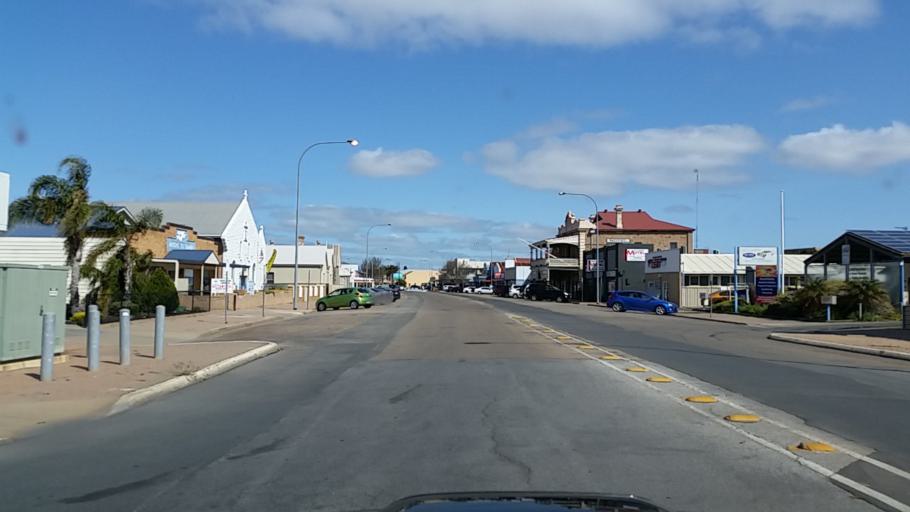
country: AU
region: South Australia
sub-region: Port Pirie City and Dists
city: Port Pirie
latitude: -33.1754
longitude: 138.0084
